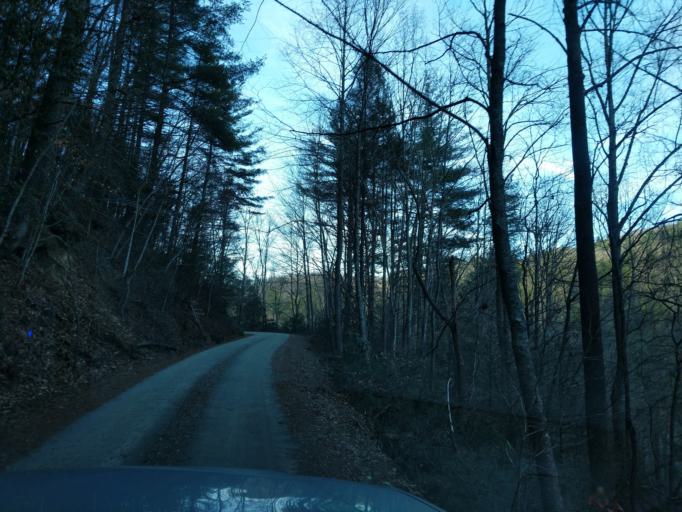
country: US
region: North Carolina
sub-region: Haywood County
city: Cove Creek
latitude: 35.7307
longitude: -83.0267
